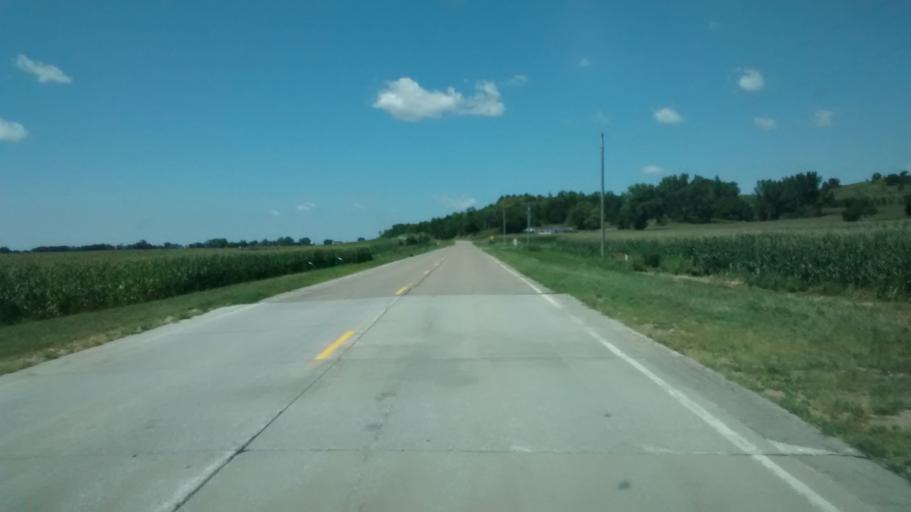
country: US
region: Iowa
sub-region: Woodbury County
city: Moville
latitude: 42.2658
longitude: -96.0567
